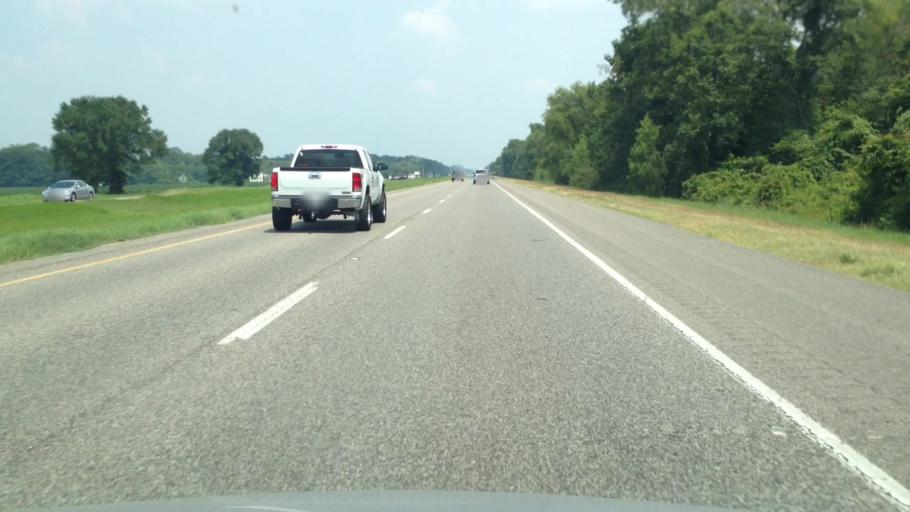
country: US
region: Louisiana
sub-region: West Baton Rouge Parish
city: Erwinville
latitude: 30.5209
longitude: -91.3715
